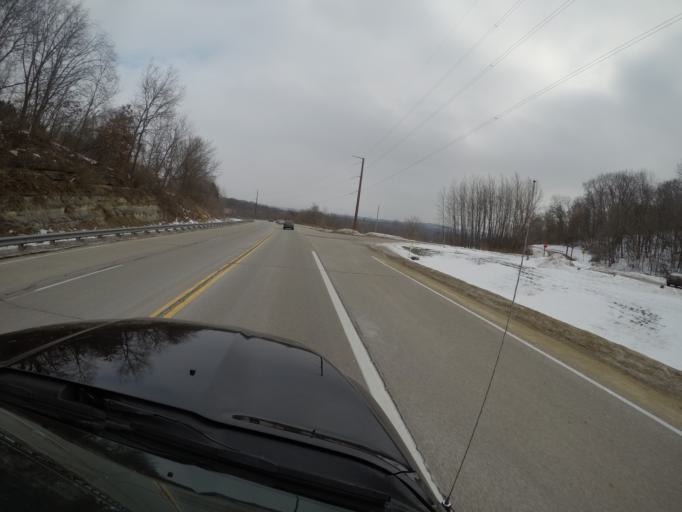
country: US
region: Wisconsin
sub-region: Trempealeau County
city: Galesville
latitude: 44.0712
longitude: -91.3216
